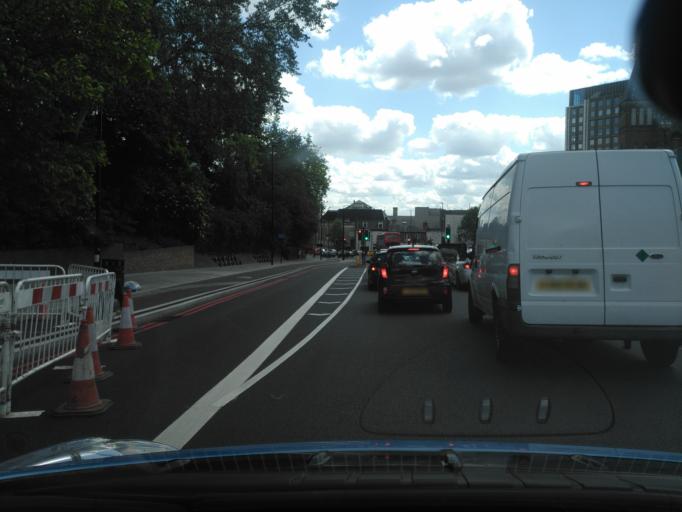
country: GB
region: England
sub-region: Greater London
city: Crouch End
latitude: 51.5676
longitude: -0.1357
